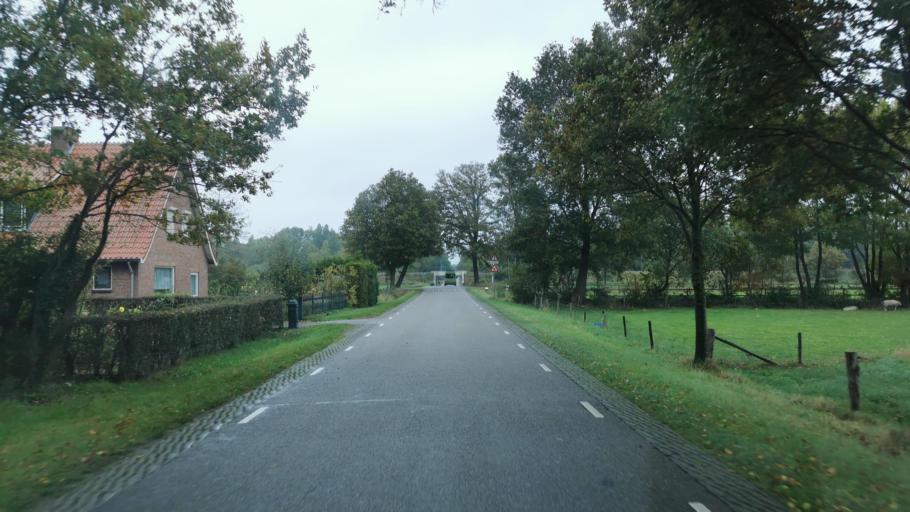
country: NL
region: Overijssel
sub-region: Gemeente Losser
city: Losser
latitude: 52.3063
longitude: 7.0162
